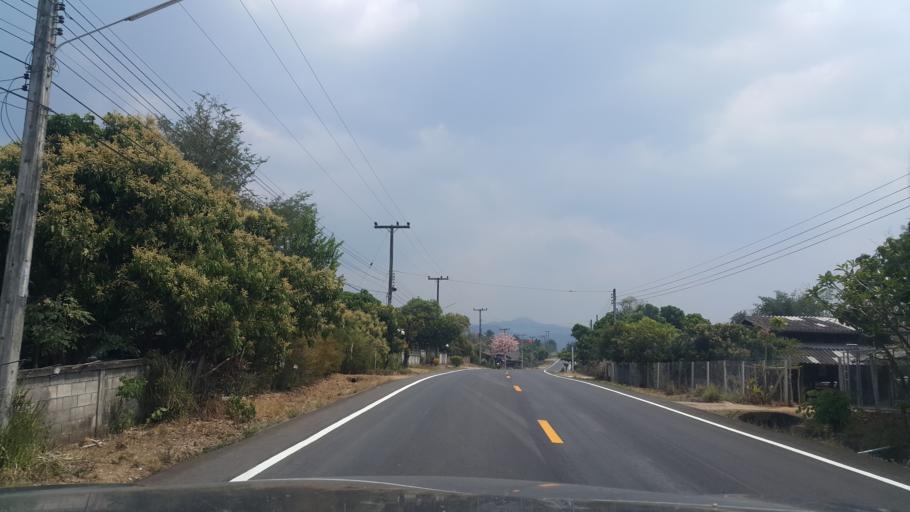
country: TH
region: Lamphun
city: Ban Hong
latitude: 18.2620
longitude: 98.9417
